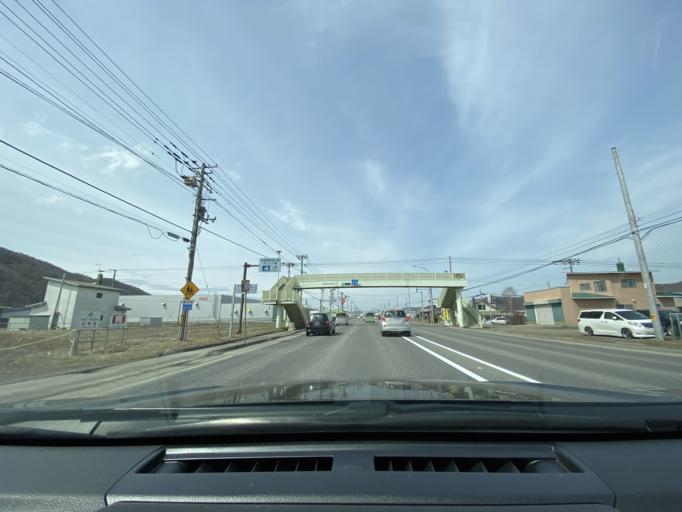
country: JP
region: Hokkaido
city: Kitami
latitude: 43.8031
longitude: 143.8084
